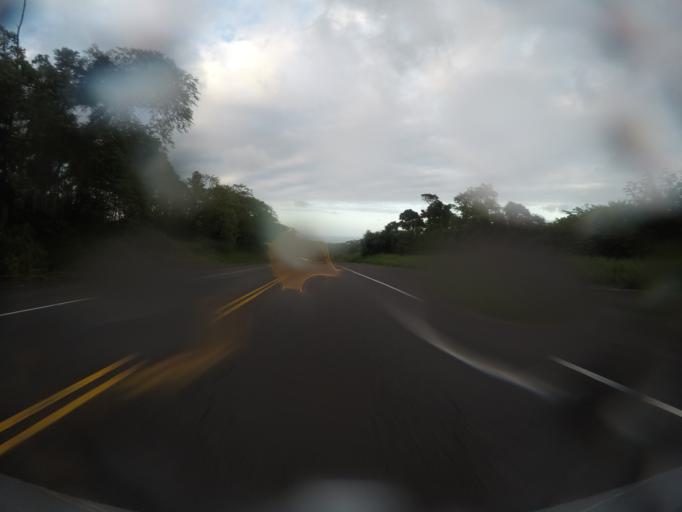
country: US
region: Hawaii
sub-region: Hawaii County
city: Hilo
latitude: 19.6851
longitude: -155.1191
